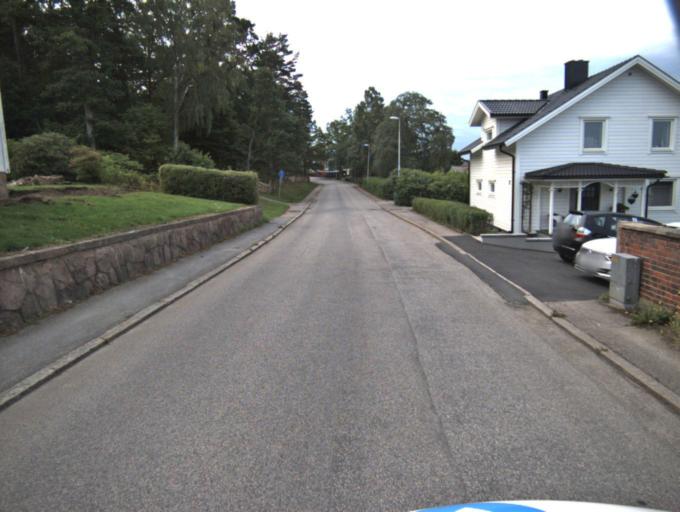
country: SE
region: Vaestra Goetaland
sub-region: Ulricehamns Kommun
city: Ulricehamn
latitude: 57.7855
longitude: 13.4092
